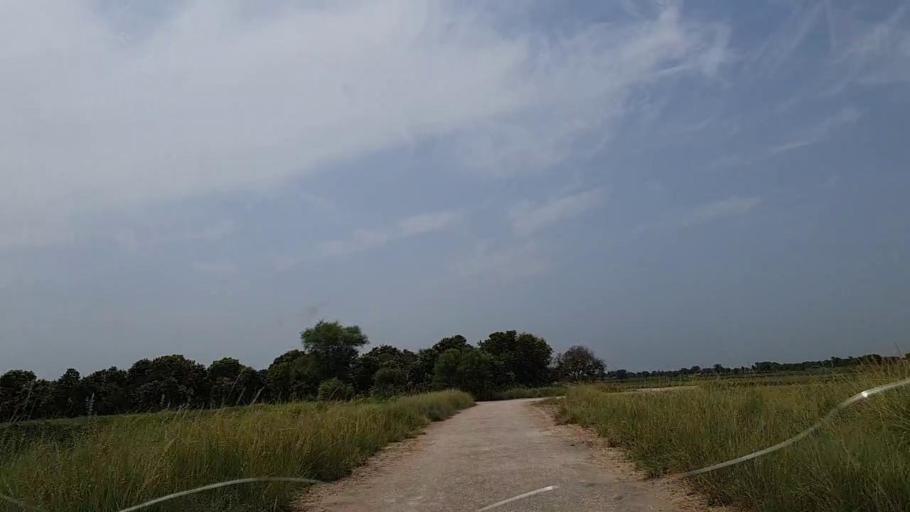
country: PK
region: Sindh
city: Tharu Shah
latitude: 26.8951
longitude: 68.0792
